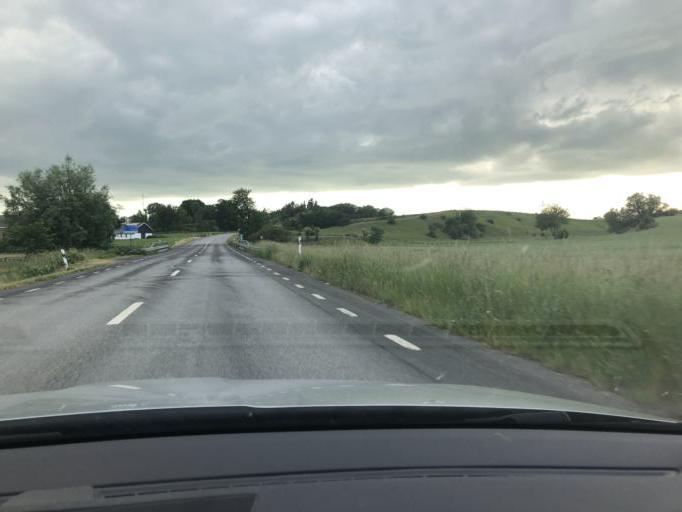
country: SE
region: Skane
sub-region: Simrishamns Kommun
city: Simrishamn
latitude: 55.5325
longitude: 14.2713
